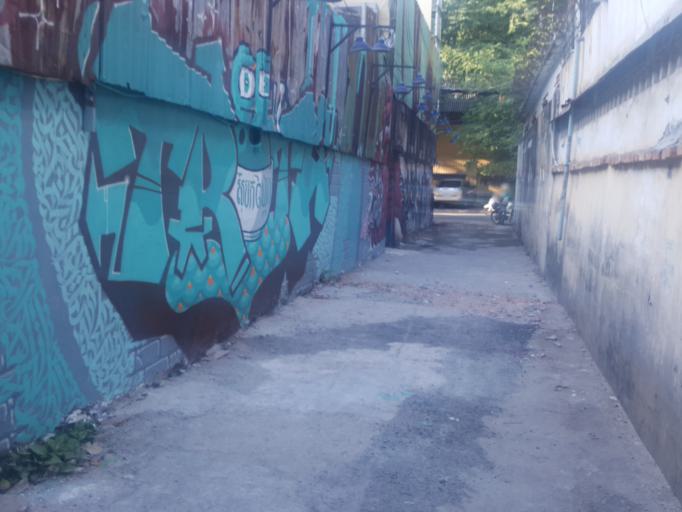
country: KH
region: Phnom Penh
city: Phnom Penh
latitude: 11.5604
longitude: 104.9304
